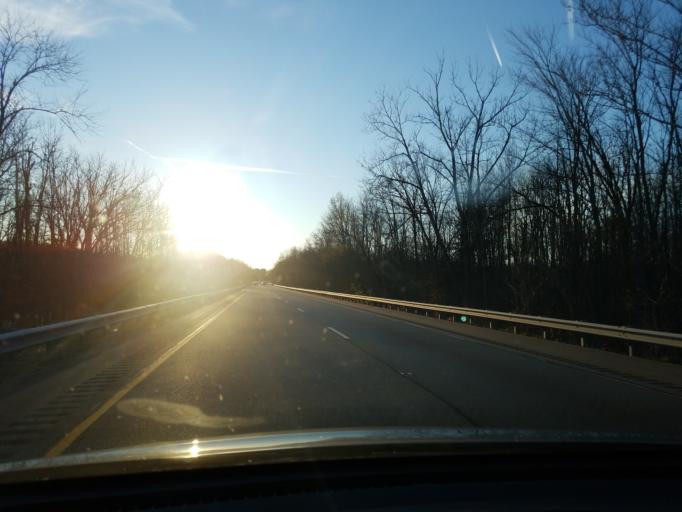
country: US
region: Indiana
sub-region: Warrick County
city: Chandler
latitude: 38.1737
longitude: -87.4212
